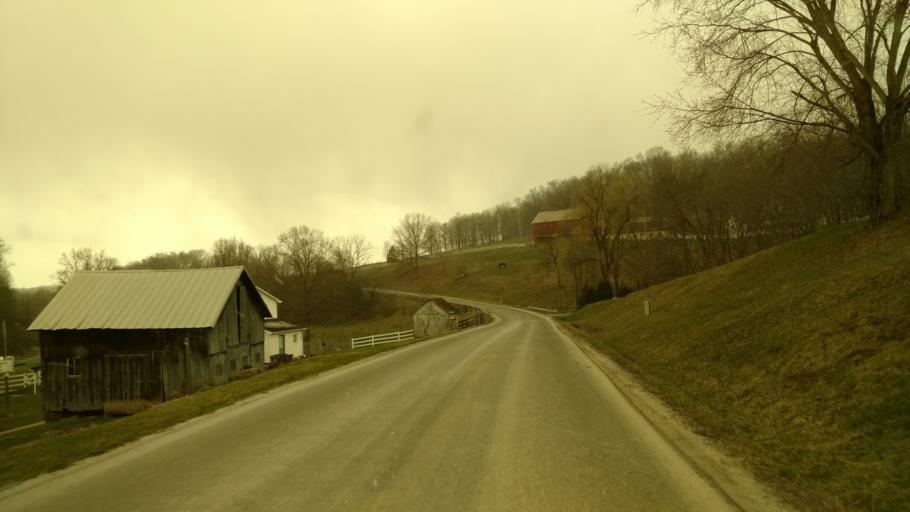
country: US
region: Ohio
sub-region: Tuscarawas County
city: Sugarcreek
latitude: 40.4455
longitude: -81.7940
